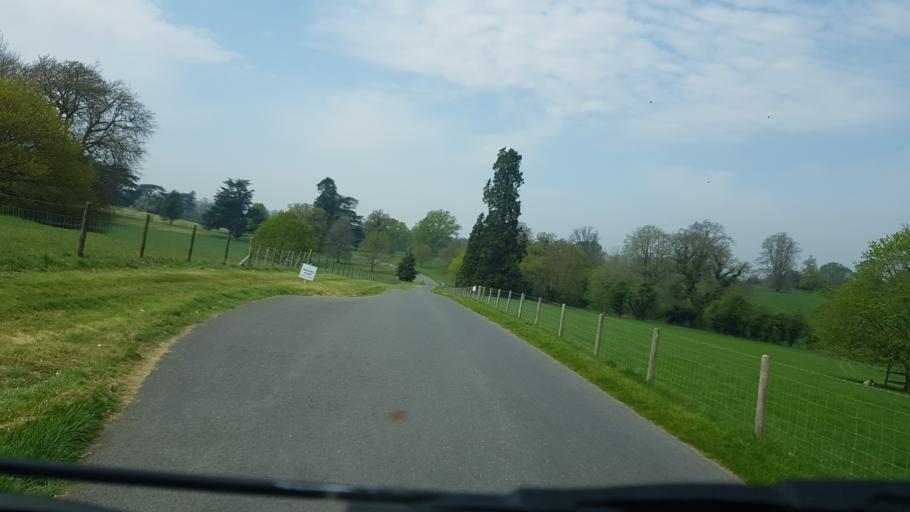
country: GB
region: England
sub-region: Hampshire
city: Highclere
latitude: 51.3304
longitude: -1.3516
